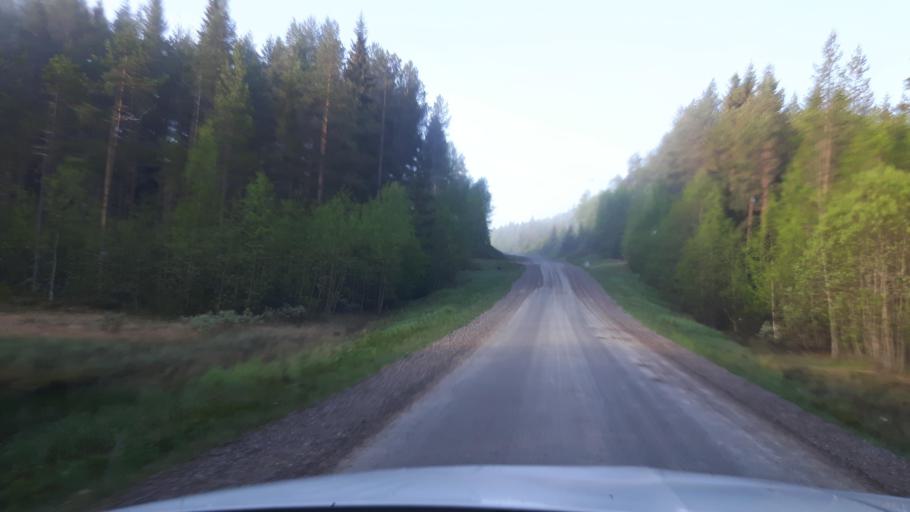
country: SE
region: Gaevleborg
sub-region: Ljusdals Kommun
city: Farila
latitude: 62.0342
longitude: 15.8214
